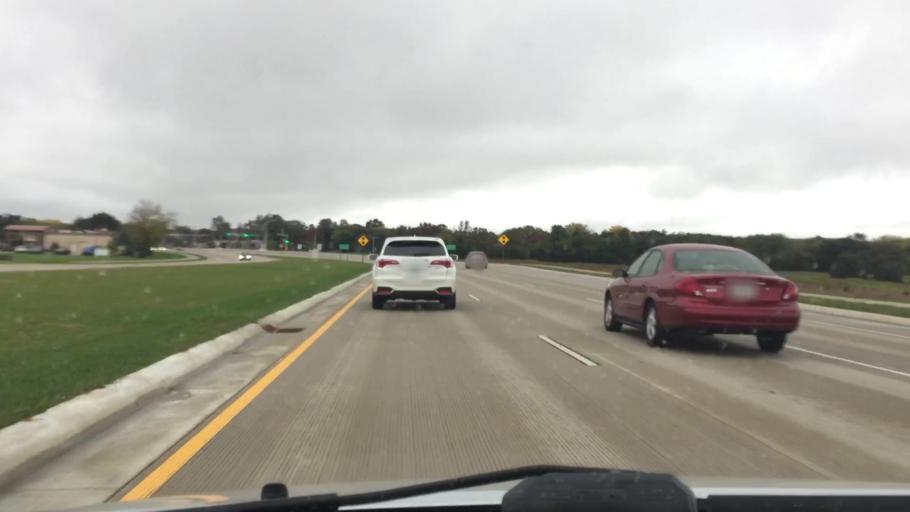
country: US
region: Wisconsin
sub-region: Waukesha County
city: Oconomowoc
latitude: 43.0841
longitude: -88.4704
